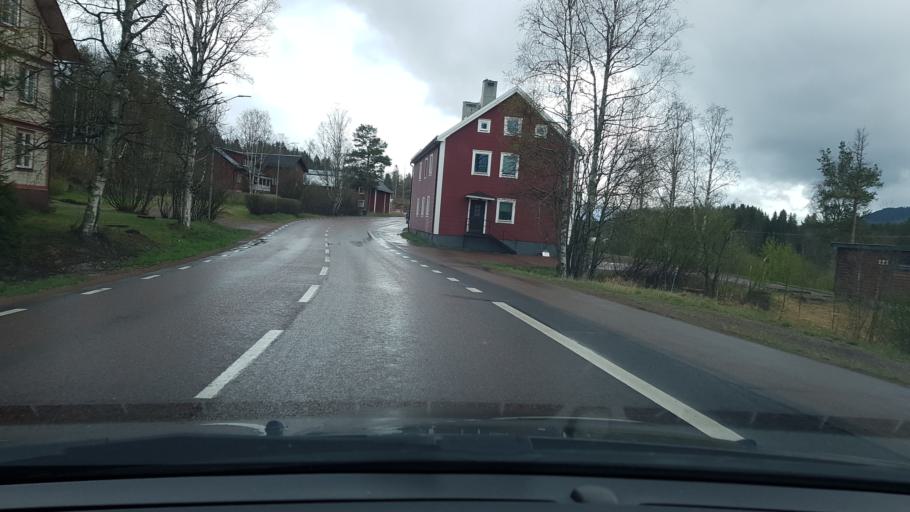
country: SE
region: Dalarna
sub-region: Malung-Saelens kommun
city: Malung
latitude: 61.0907
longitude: 13.3197
